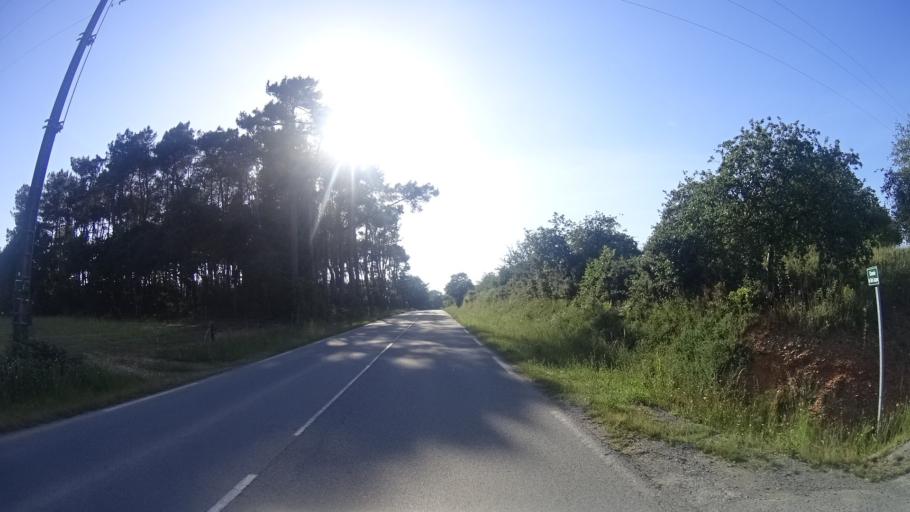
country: FR
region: Brittany
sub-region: Departement du Morbihan
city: Rieux
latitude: 47.6087
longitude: -2.1335
